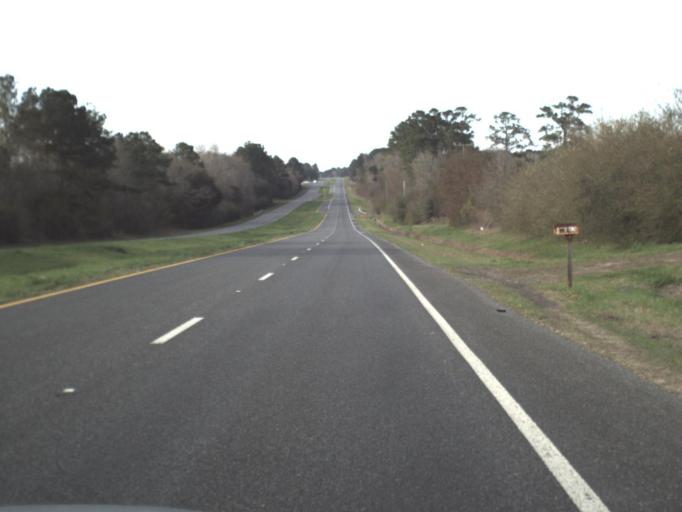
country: US
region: Florida
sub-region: Jefferson County
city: Monticello
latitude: 30.5726
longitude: -83.8698
